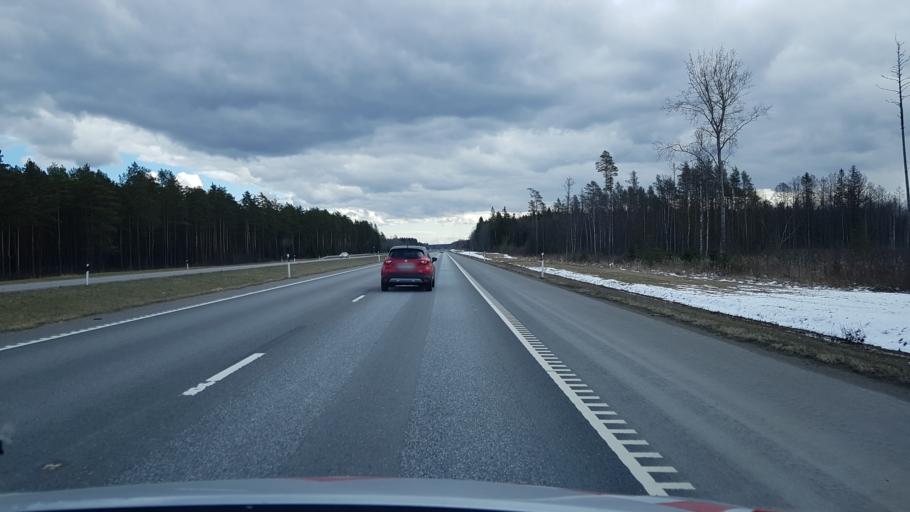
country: EE
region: Harju
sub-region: Loksa linn
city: Loksa
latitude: 59.4558
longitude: 25.8810
